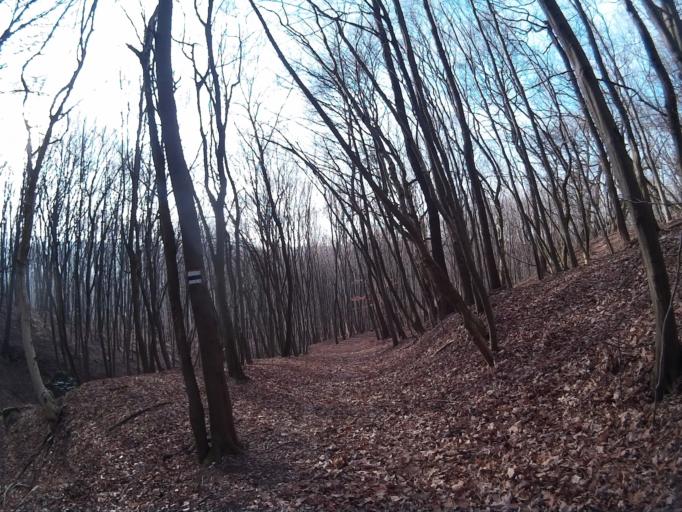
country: HU
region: Komarom-Esztergom
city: Oroszlany
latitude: 47.4816
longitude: 18.3996
